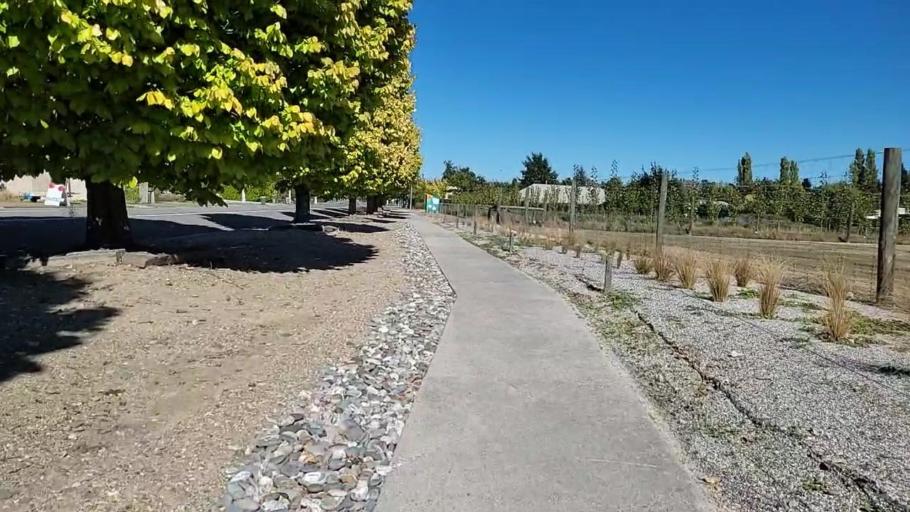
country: NZ
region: Otago
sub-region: Queenstown-Lakes District
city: Wanaka
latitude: -45.0988
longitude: 169.5976
